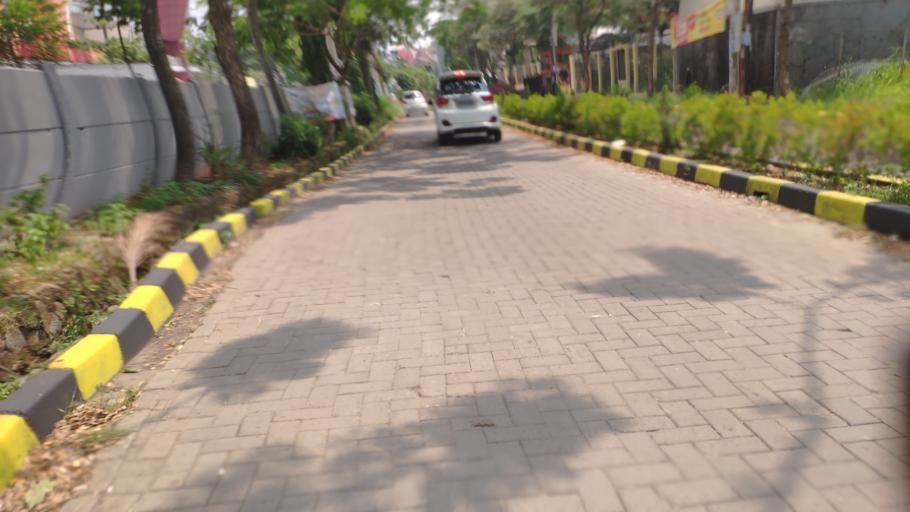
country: ID
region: West Java
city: Sawangan
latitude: -6.3958
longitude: 106.7931
